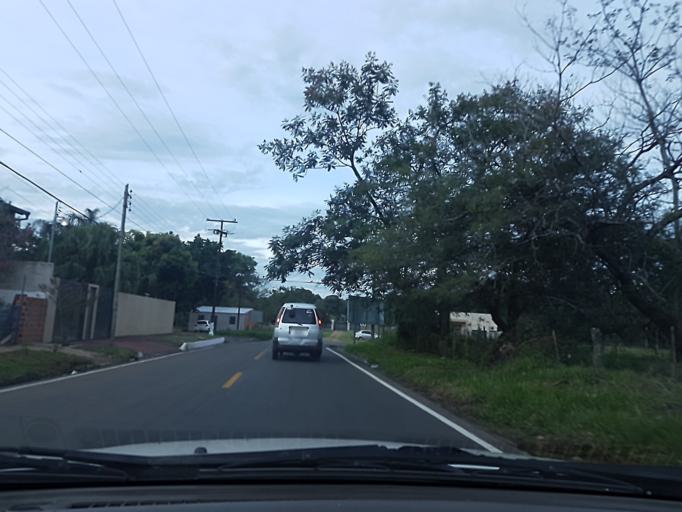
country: PY
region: Central
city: San Lorenzo
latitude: -25.2660
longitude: -57.4742
